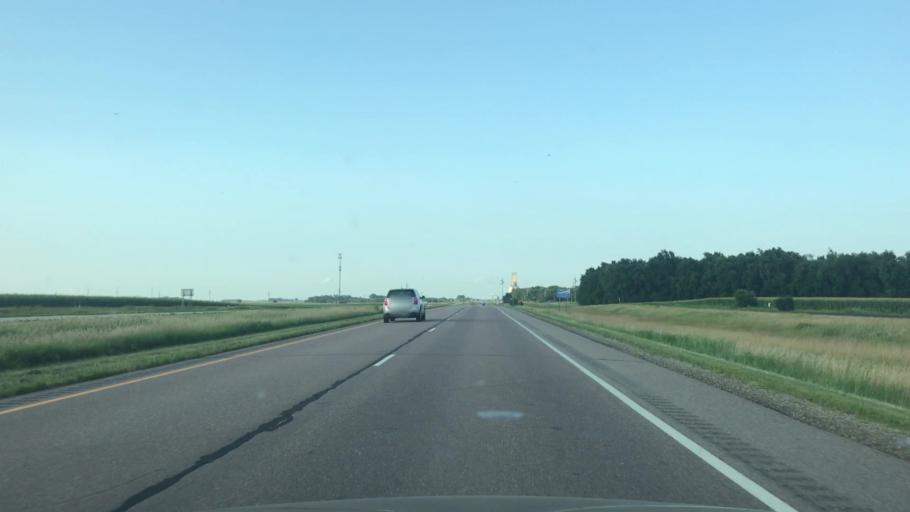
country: US
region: Minnesota
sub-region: Jackson County
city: Lakefield
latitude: 43.7571
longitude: -95.3813
